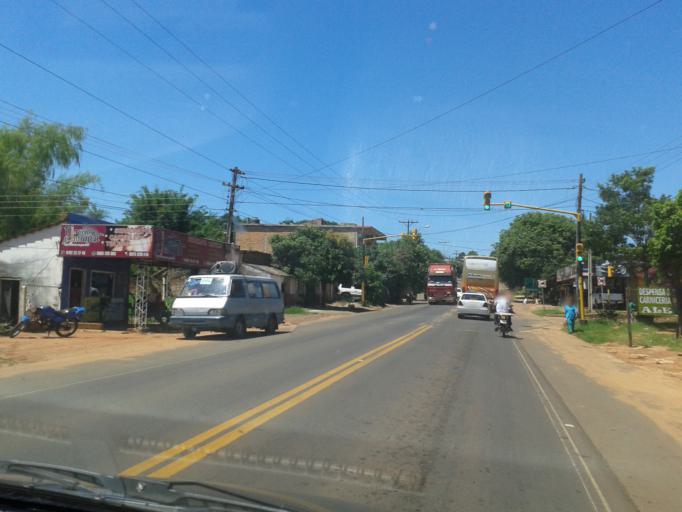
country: PY
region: Misiones
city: Santa Maria
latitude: -26.8853
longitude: -57.0147
